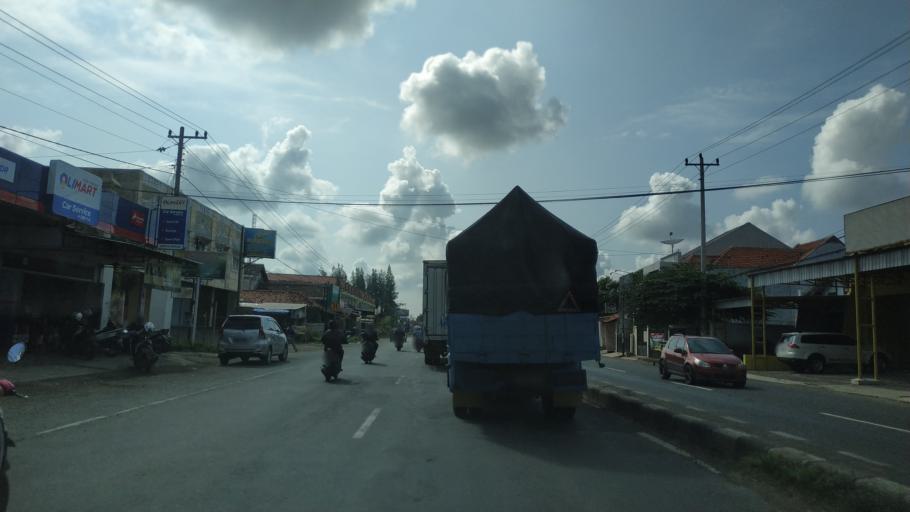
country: ID
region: Central Java
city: Comal
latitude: -6.8982
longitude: 109.5338
